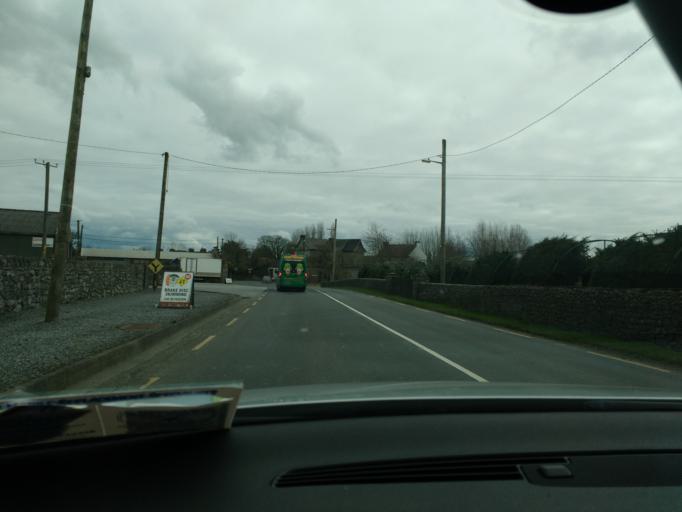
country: IE
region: Leinster
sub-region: Kilkenny
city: Ballyragget
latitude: 52.7341
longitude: -7.4024
